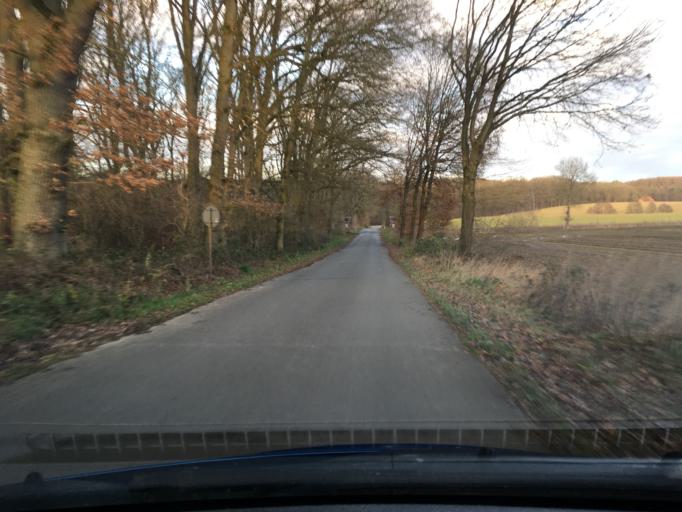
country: DE
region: Lower Saxony
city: Amelinghausen
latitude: 53.1378
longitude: 10.1879
